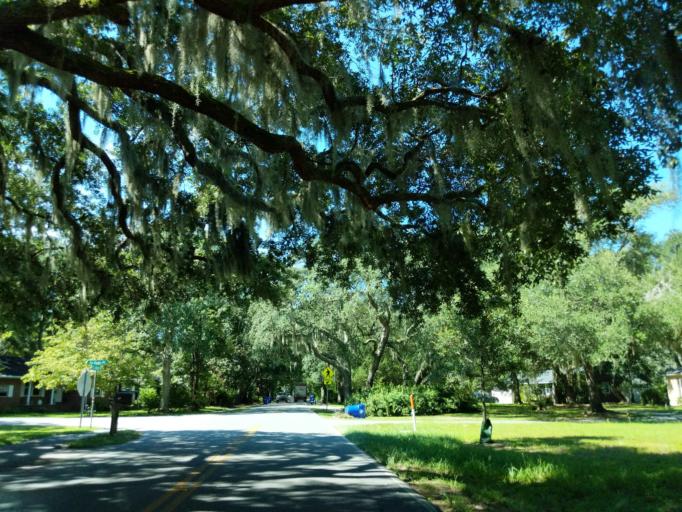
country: US
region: South Carolina
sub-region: Charleston County
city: Charleston
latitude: 32.7374
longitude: -79.9224
